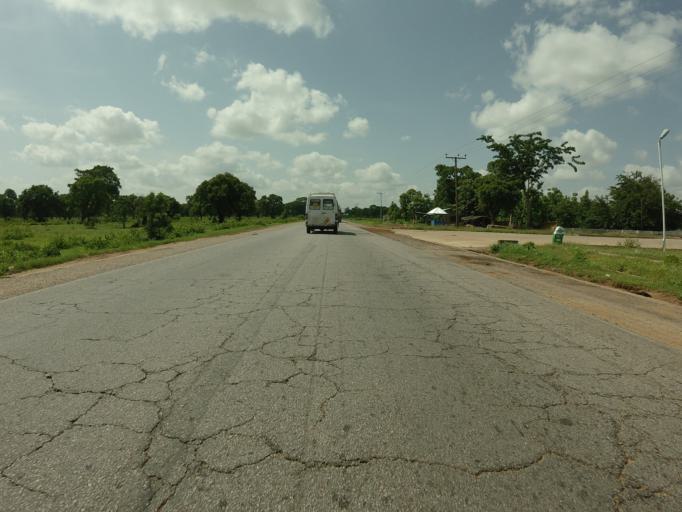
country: GH
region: Northern
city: Savelugu
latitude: 9.5716
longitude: -0.8349
